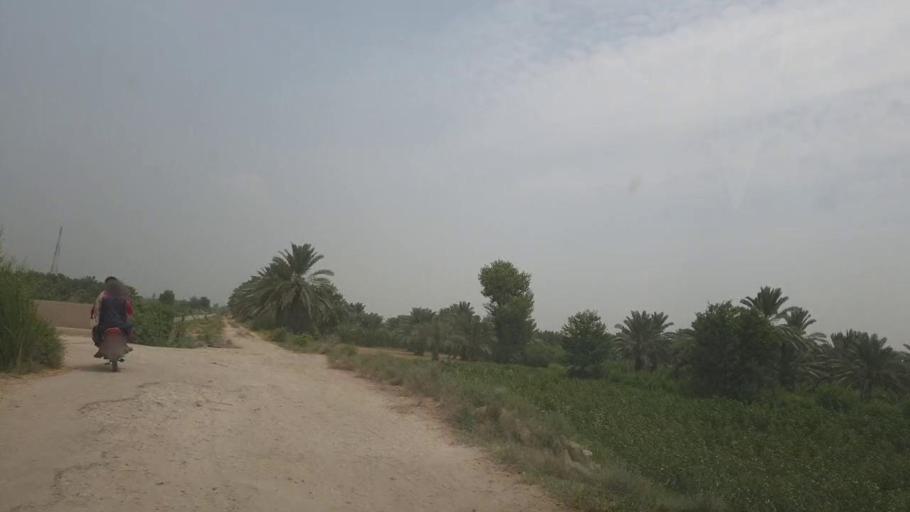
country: PK
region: Sindh
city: Kot Diji
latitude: 27.4443
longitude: 68.6406
